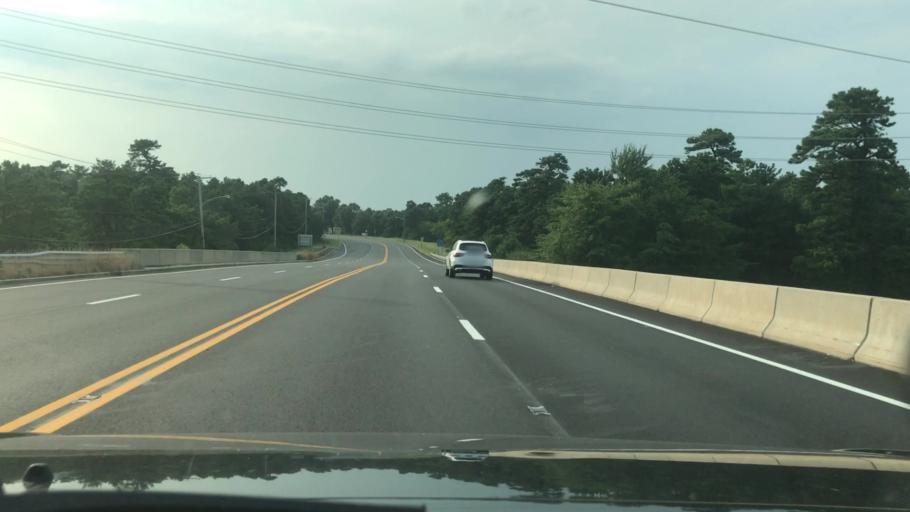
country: US
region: New Jersey
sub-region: Ocean County
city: Leisure Village
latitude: 40.0665
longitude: -74.1632
